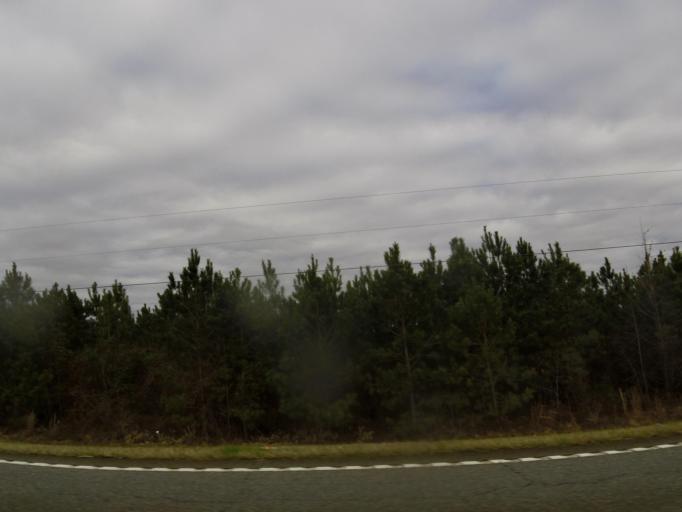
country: US
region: Georgia
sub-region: Quitman County
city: Georgetown
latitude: 31.8477
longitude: -85.0092
